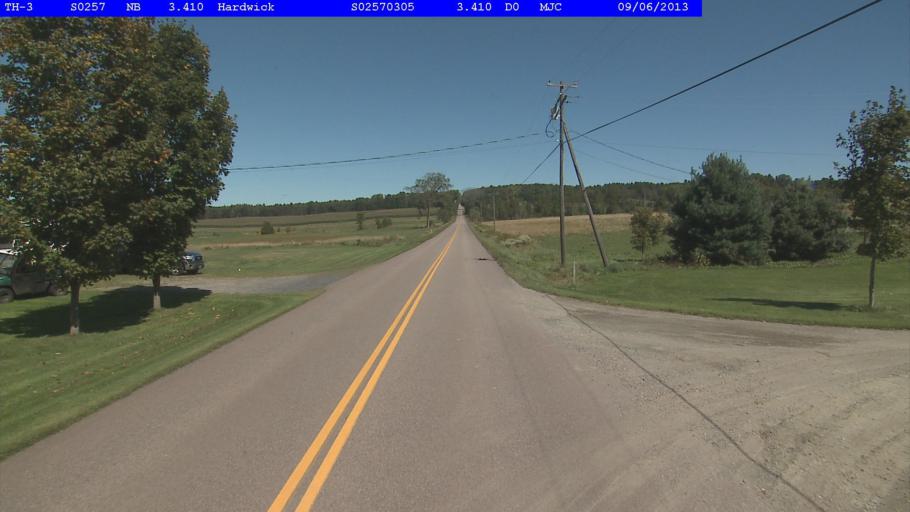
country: US
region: Vermont
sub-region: Caledonia County
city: Hardwick
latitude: 44.5383
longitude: -72.3295
